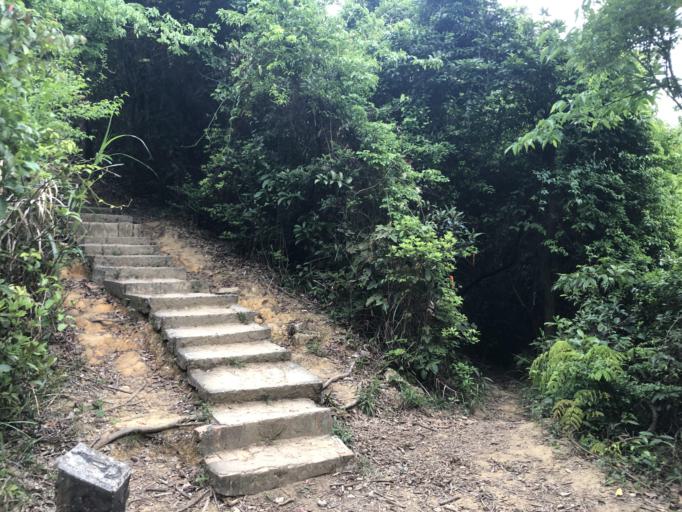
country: HK
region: Sha Tin
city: Sha Tin
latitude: 22.3804
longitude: 114.1500
